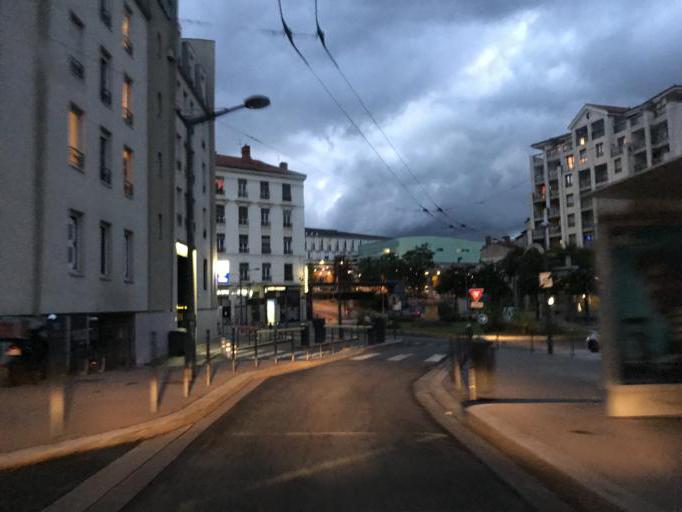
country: FR
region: Rhone-Alpes
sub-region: Departement du Rhone
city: Caluire-et-Cuire
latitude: 45.7813
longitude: 4.8334
